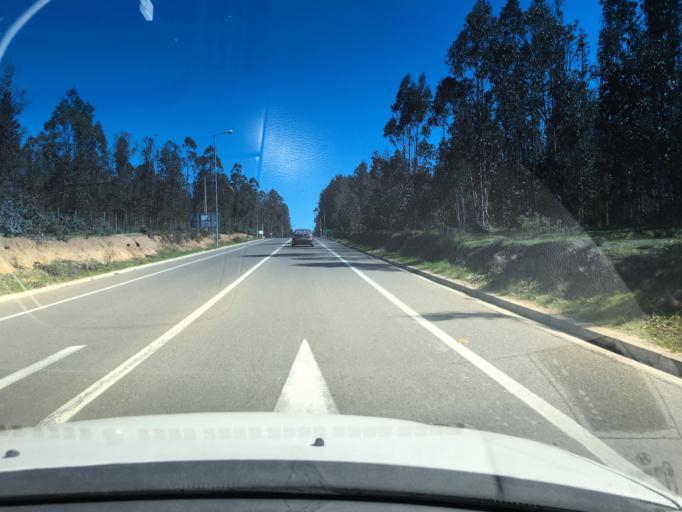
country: CL
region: Valparaiso
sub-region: San Antonio Province
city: El Tabo
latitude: -33.4265
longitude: -71.6376
